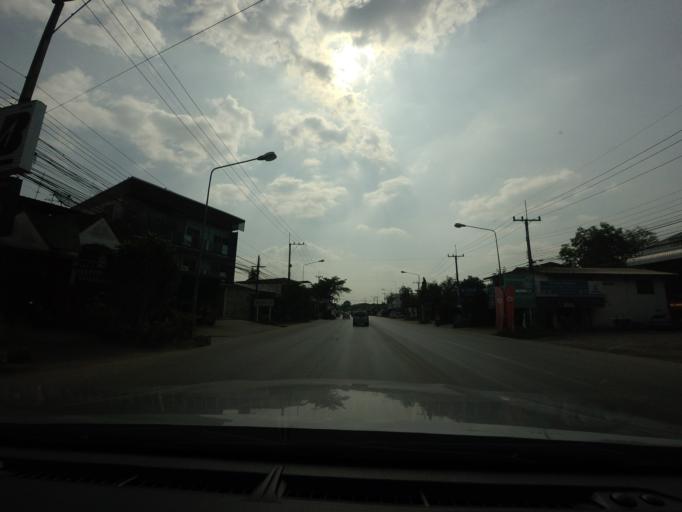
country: TH
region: Phitsanulok
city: Bang Rakam
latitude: 16.7514
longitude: 100.1139
